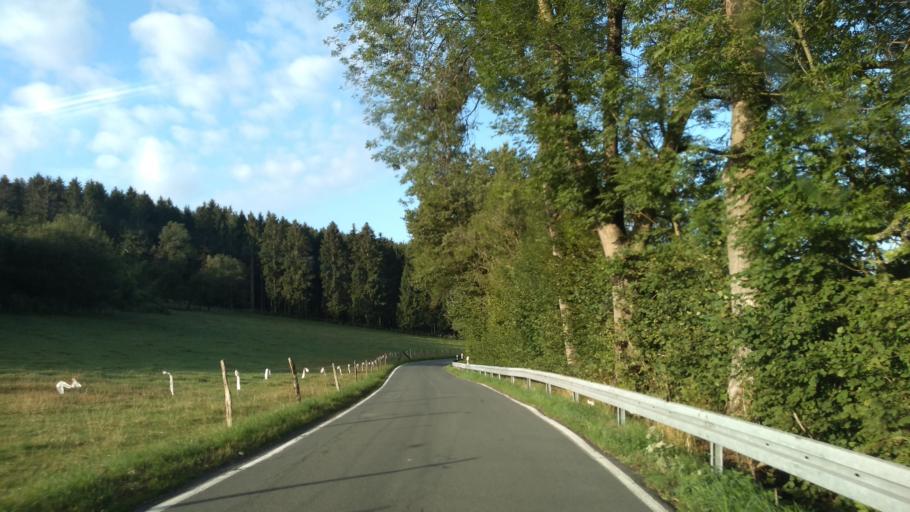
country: DE
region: North Rhine-Westphalia
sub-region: Regierungsbezirk Koln
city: Gummersbach
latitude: 51.0314
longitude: 7.5324
